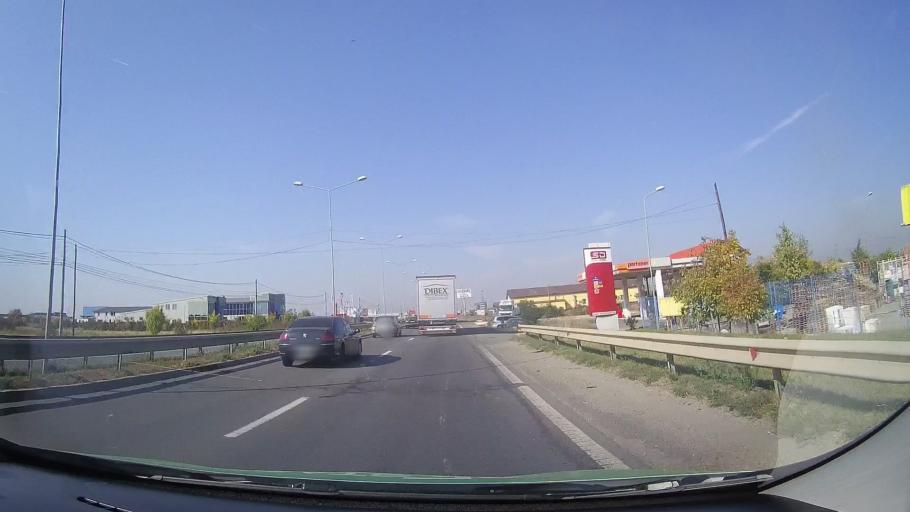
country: RO
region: Bihor
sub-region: Comuna Biharea
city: Oradea
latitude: 47.0476
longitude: 21.8953
